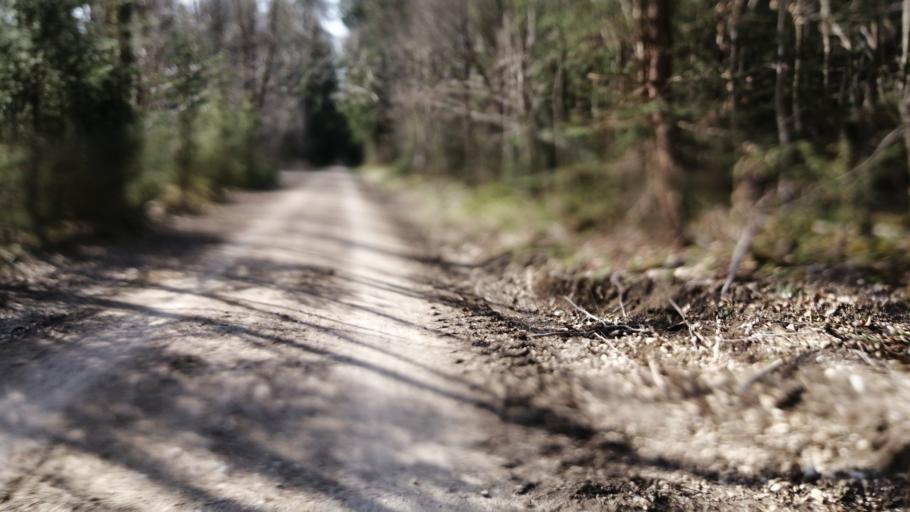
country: DE
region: Bavaria
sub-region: Upper Bavaria
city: Sauerlach
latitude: 48.0004
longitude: 11.6280
